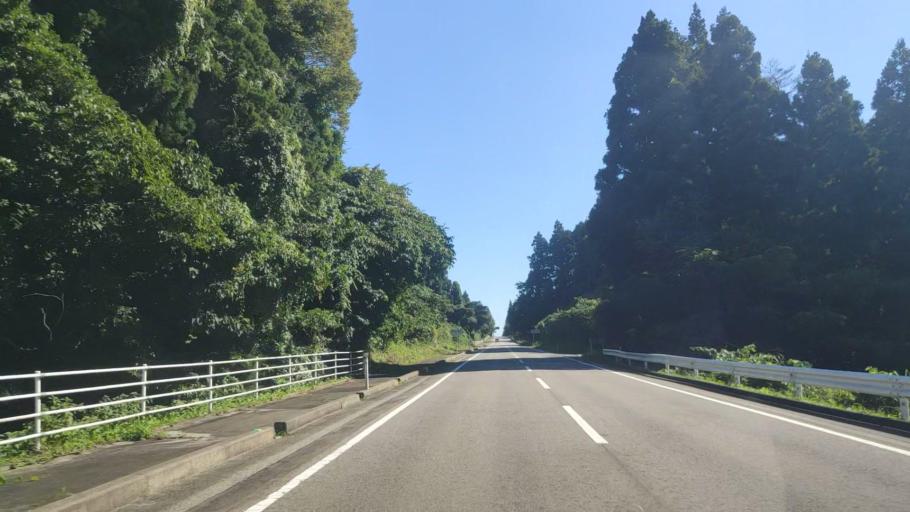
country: JP
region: Ishikawa
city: Nanao
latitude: 37.3742
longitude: 137.2347
